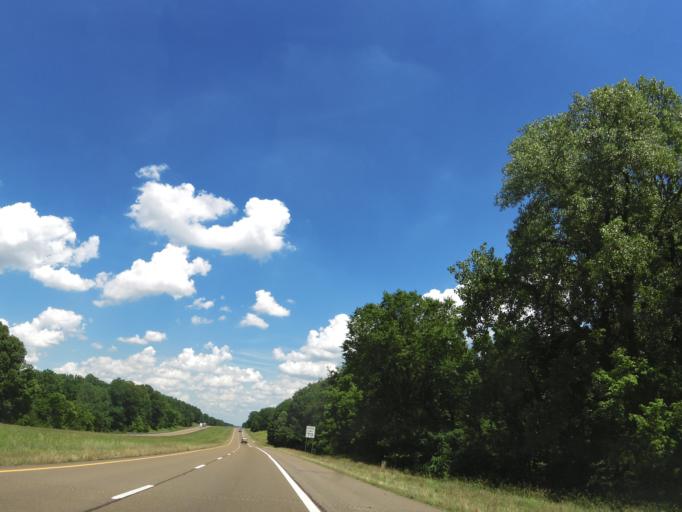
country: US
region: Tennessee
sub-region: Dyer County
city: Dyersburg
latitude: 36.0695
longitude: -89.4463
